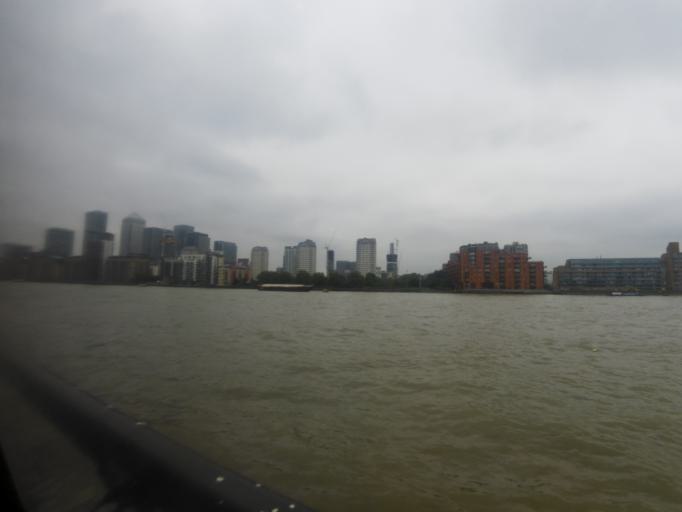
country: GB
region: England
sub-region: Greater London
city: Poplar
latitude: 51.4960
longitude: -0.0312
